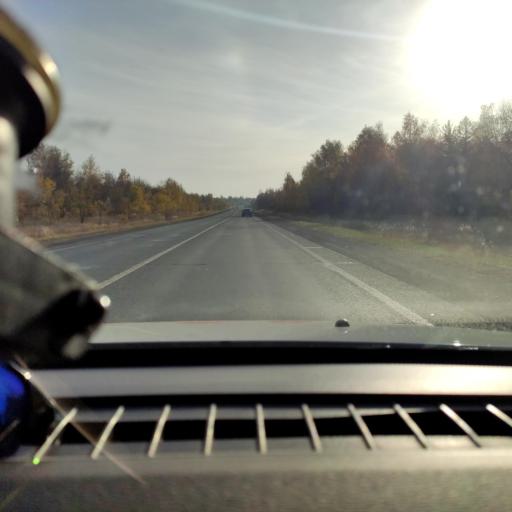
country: RU
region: Samara
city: Chapayevsk
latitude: 52.9933
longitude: 49.8255
